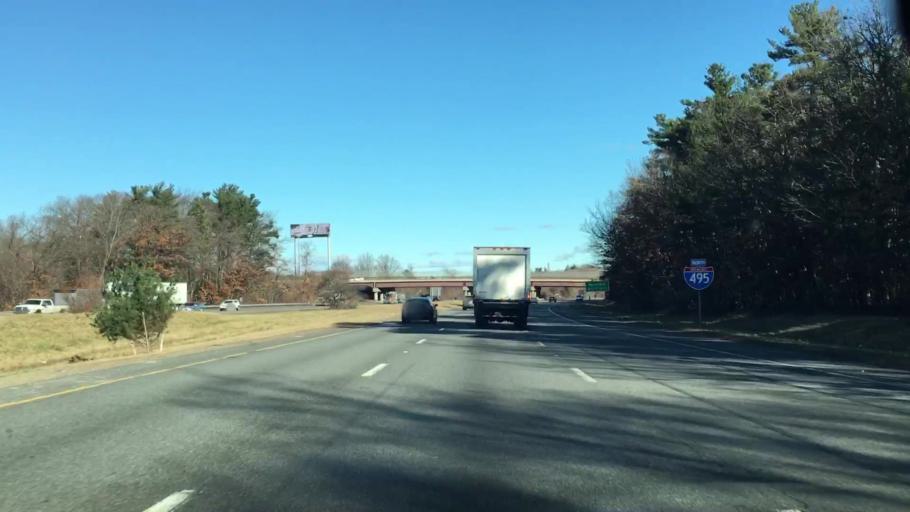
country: US
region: Massachusetts
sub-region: Essex County
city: Lawrence
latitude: 42.7429
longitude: -71.1402
